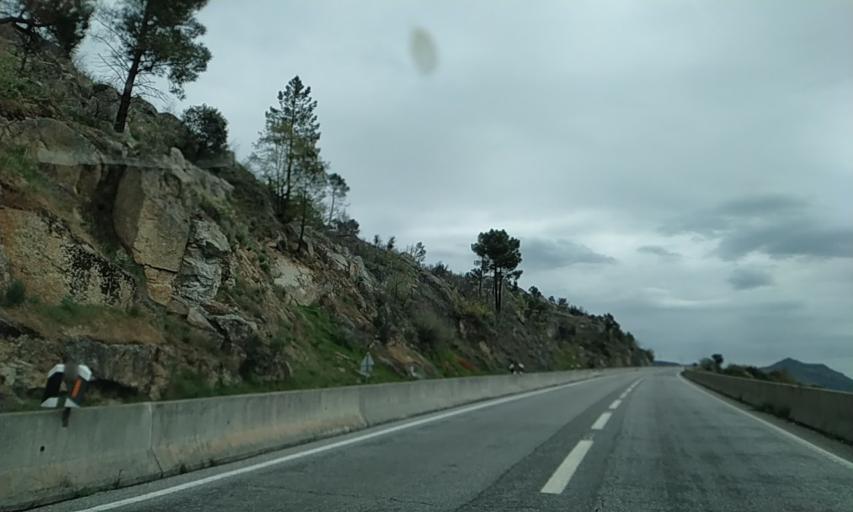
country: PT
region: Guarda
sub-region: Guarda
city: Guarda
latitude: 40.6082
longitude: -7.2829
